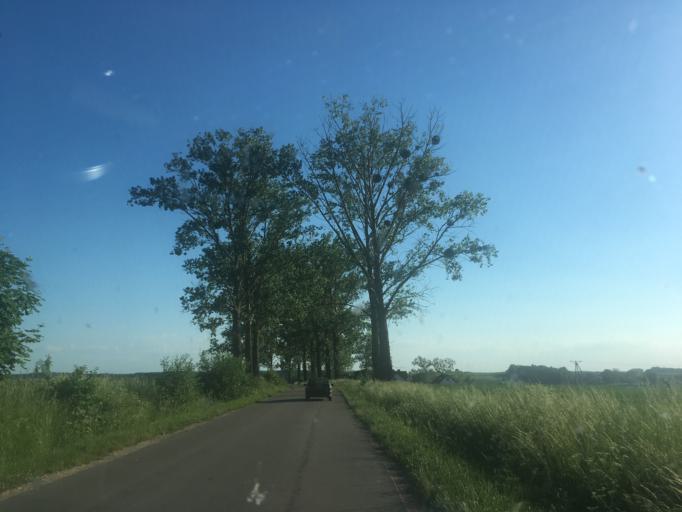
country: PL
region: Warmian-Masurian Voivodeship
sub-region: Powiat ostrodzki
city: Ostroda
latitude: 53.6755
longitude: 20.0404
